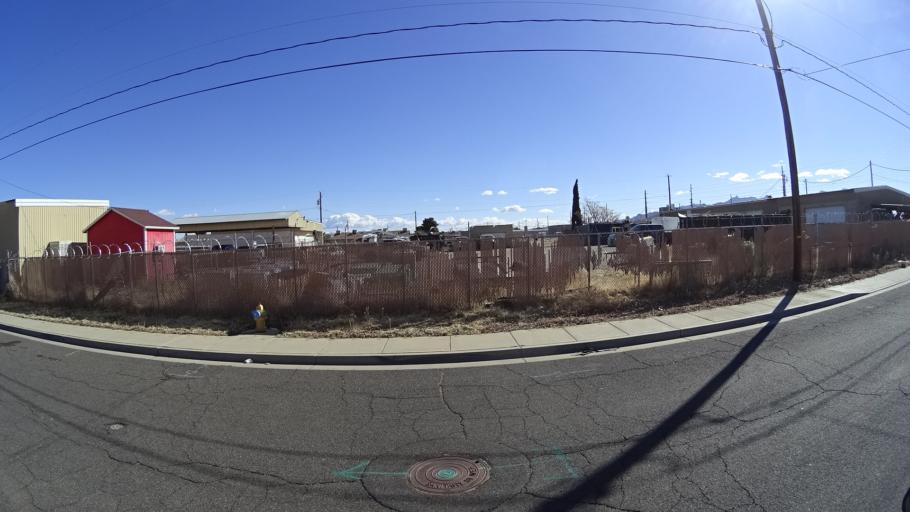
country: US
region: Arizona
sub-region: Mohave County
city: New Kingman-Butler
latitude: 35.2260
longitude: -114.0267
